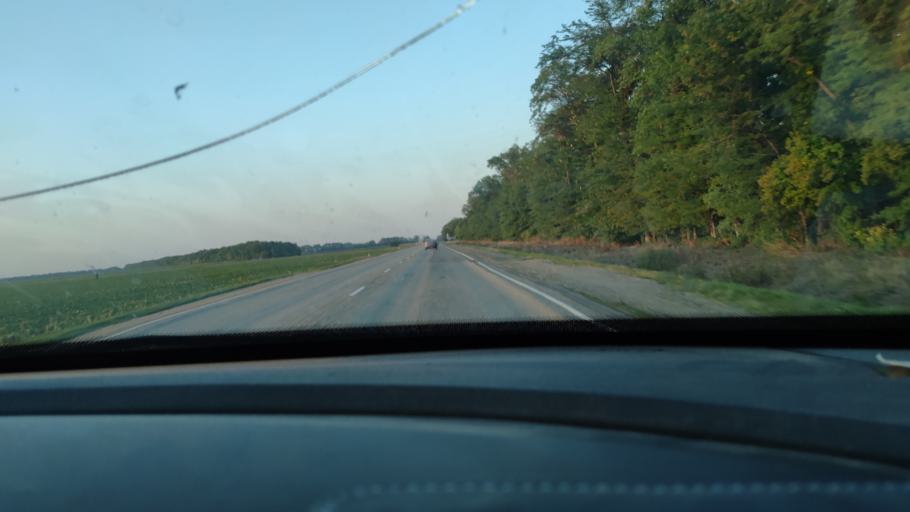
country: RU
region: Krasnodarskiy
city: Starominskaya
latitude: 46.4595
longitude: 39.0363
